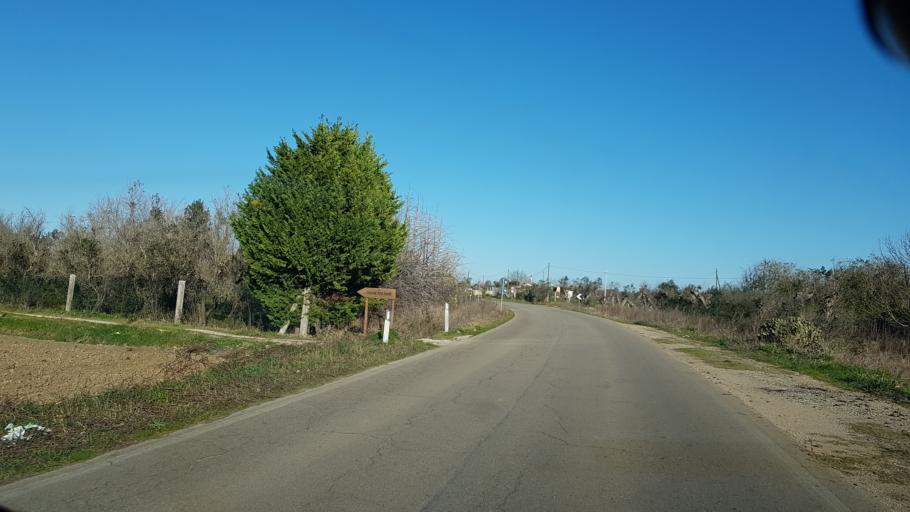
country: IT
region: Apulia
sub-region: Provincia di Lecce
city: Melissano
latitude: 39.9977
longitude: 18.1306
